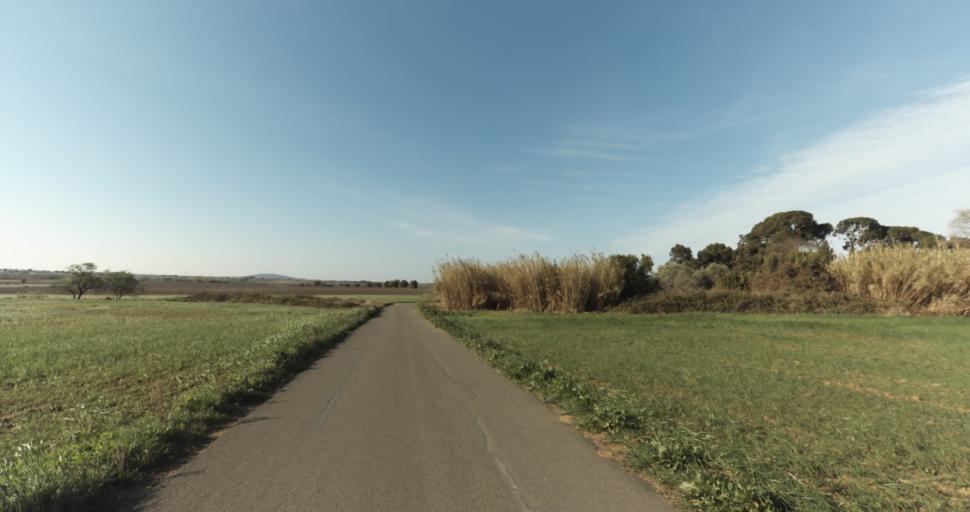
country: FR
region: Languedoc-Roussillon
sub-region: Departement de l'Herault
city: Pomerols
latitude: 43.3827
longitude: 3.5198
